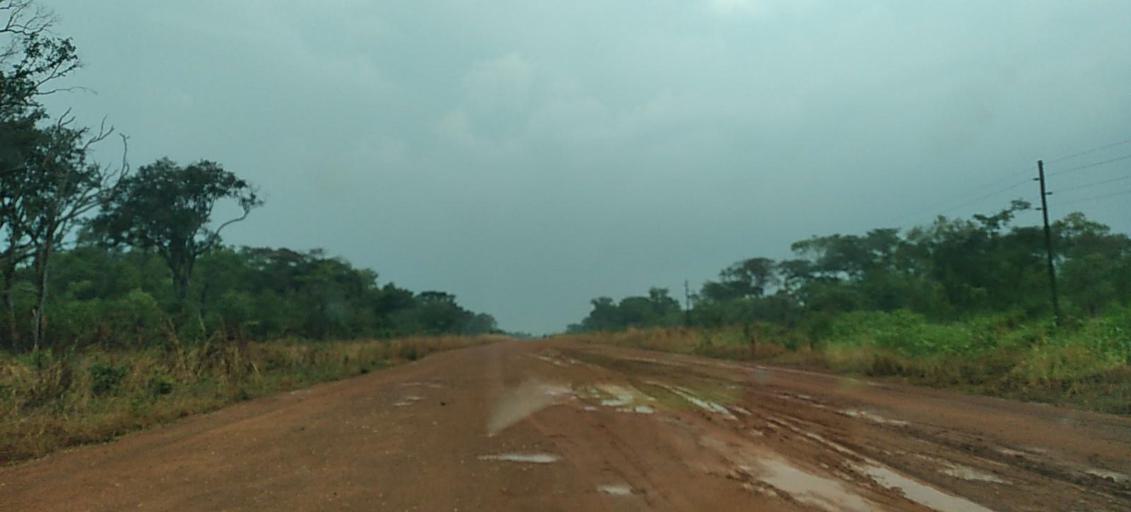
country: ZM
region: North-Western
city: Mwinilunga
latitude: -11.6079
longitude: 24.3966
